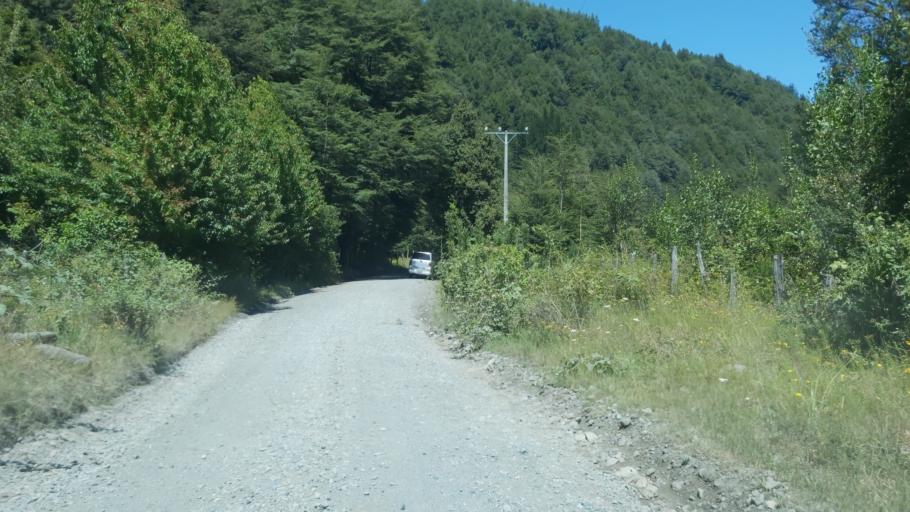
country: CL
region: Araucania
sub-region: Provincia de Cautin
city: Vilcun
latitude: -38.4729
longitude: -71.6733
